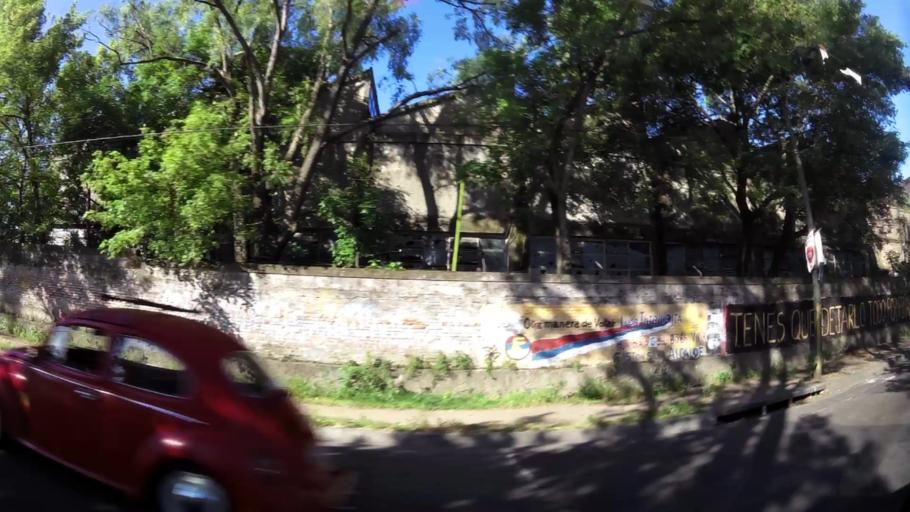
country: UY
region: Canelones
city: La Paz
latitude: -34.8238
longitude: -56.2062
